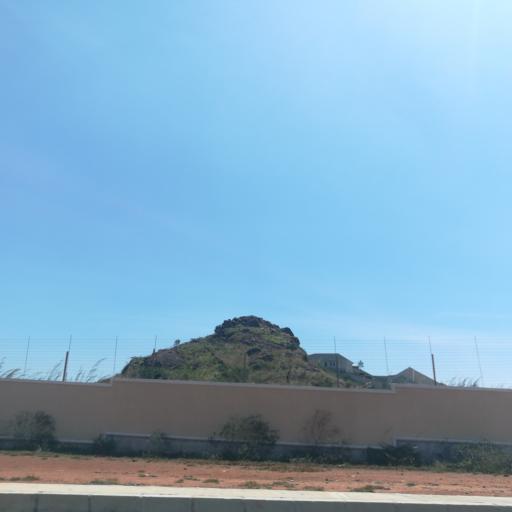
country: NG
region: Plateau
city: Bukuru
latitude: 9.8211
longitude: 8.8791
